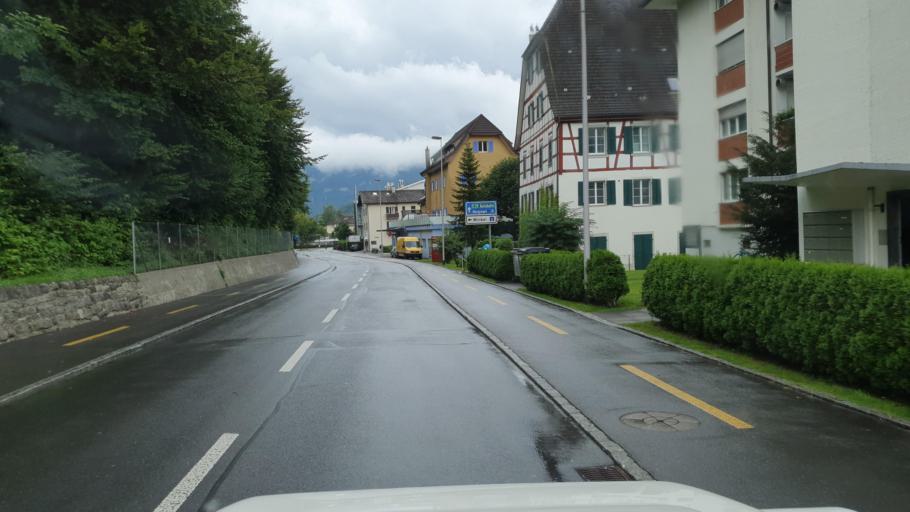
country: CH
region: Lucerne
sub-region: Lucerne-Land District
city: Horw
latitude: 47.0162
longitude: 8.3112
